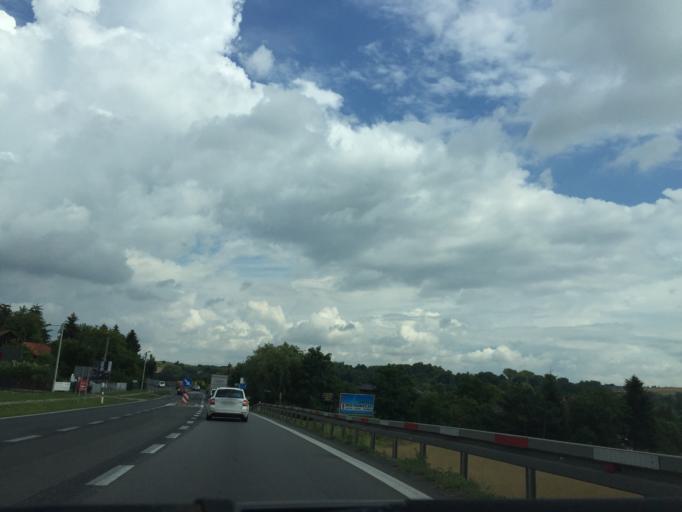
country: PL
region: Lesser Poland Voivodeship
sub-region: Powiat krakowski
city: Michalowice
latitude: 50.1477
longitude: 19.9818
